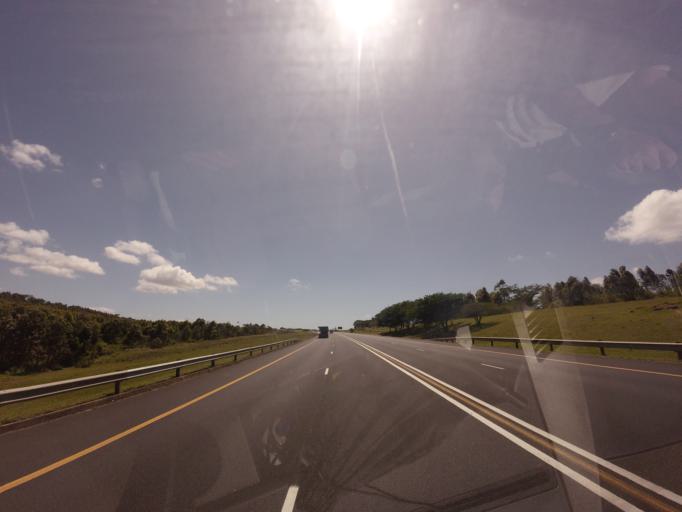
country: ZA
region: KwaZulu-Natal
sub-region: iLembe District Municipality
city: Mandeni
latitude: -29.0944
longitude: 31.5982
